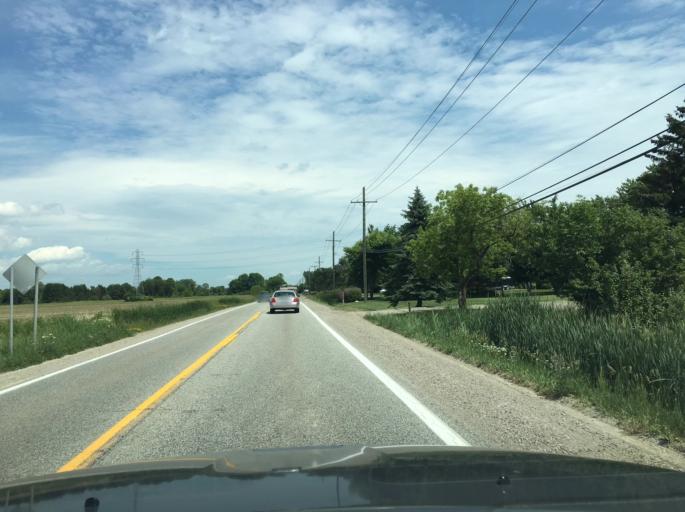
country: US
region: Michigan
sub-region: Macomb County
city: Shelby
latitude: 42.7160
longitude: -82.9756
